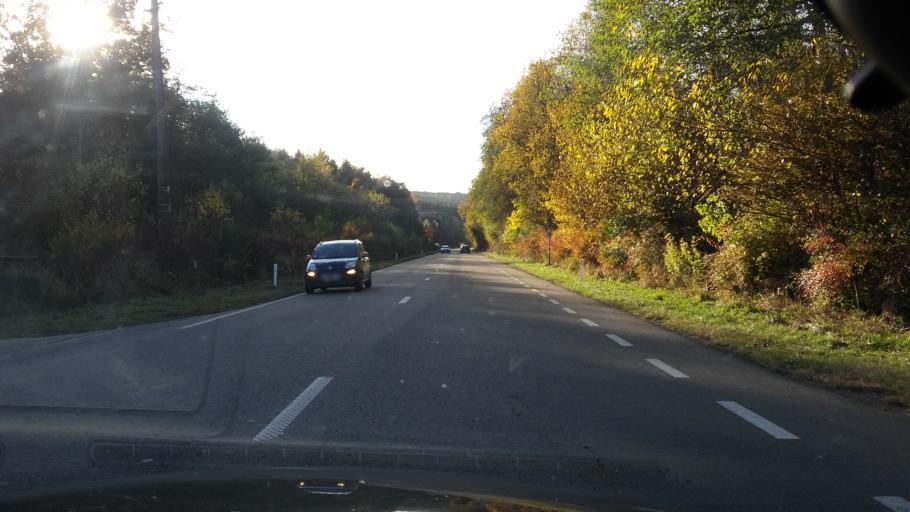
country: BE
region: Wallonia
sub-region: Province du Luxembourg
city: Bouillon
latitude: 49.7618
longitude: 5.1129
